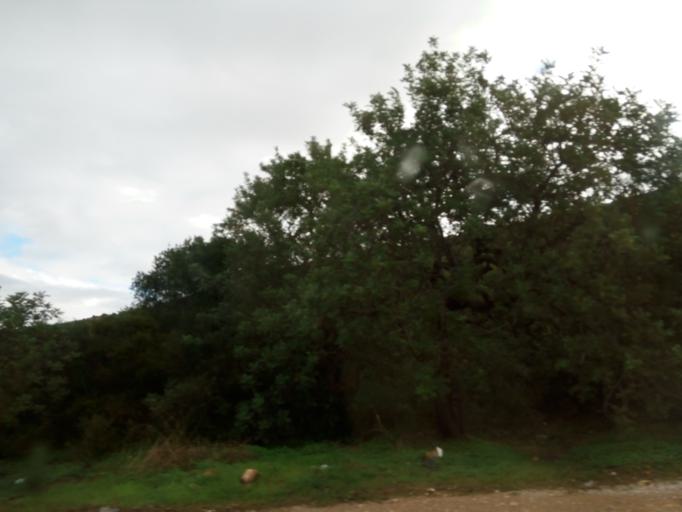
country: PT
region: Faro
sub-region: Loule
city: Loule
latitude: 37.1156
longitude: -8.0087
